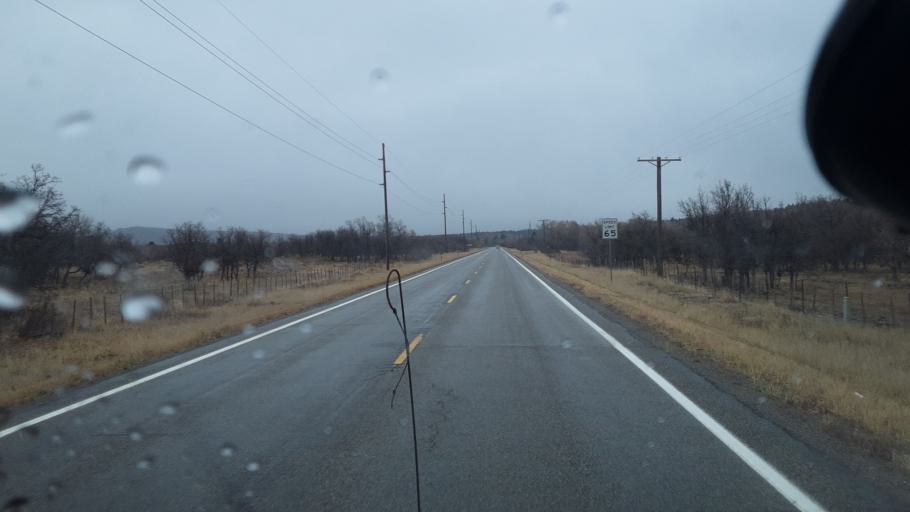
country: US
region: Colorado
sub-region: La Plata County
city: Durango
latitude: 37.2349
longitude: -108.0448
